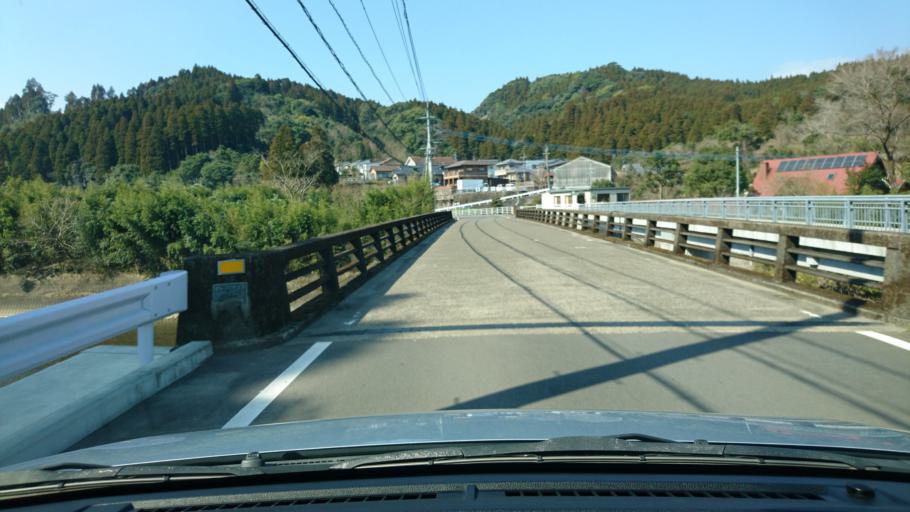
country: JP
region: Miyazaki
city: Miyazaki-shi
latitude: 31.8289
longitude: 131.4018
